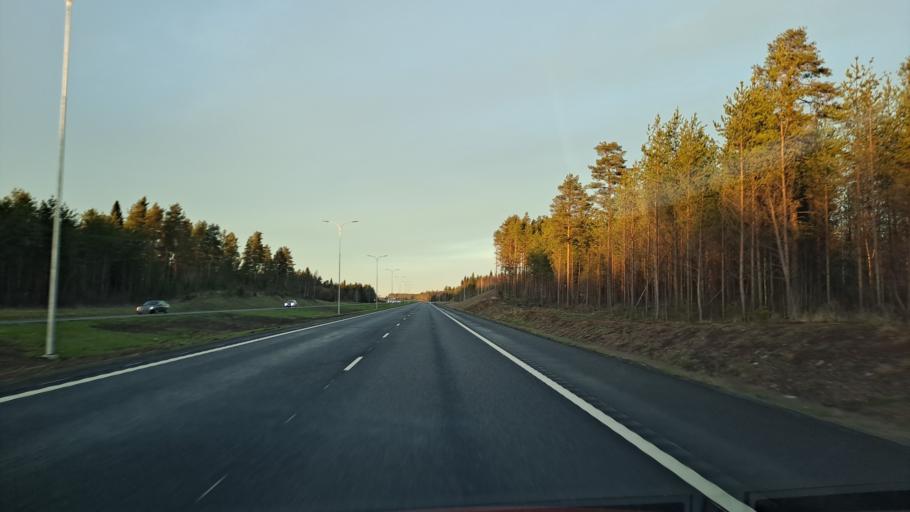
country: FI
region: Northern Ostrobothnia
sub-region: Oulu
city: Haukipudas
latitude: 65.1286
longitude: 25.4321
